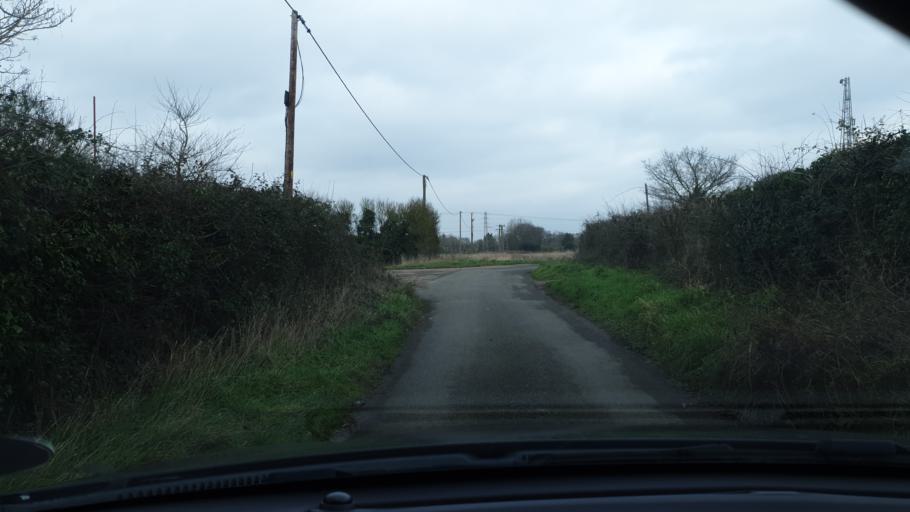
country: GB
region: England
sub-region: Essex
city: Alresford
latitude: 51.8596
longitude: 0.9924
